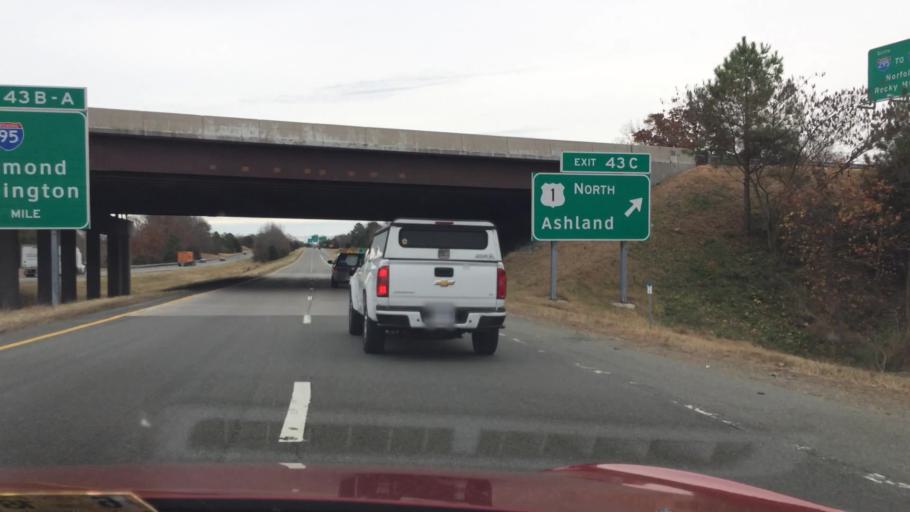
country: US
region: Virginia
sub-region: Henrico County
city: Chamberlayne
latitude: 37.6583
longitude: -77.4606
